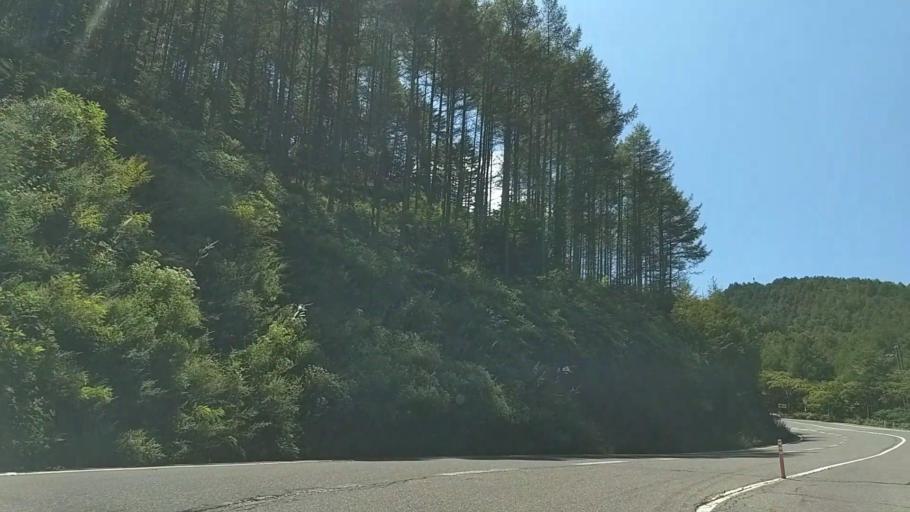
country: JP
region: Nagano
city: Suwa
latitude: 36.1135
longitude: 138.2356
